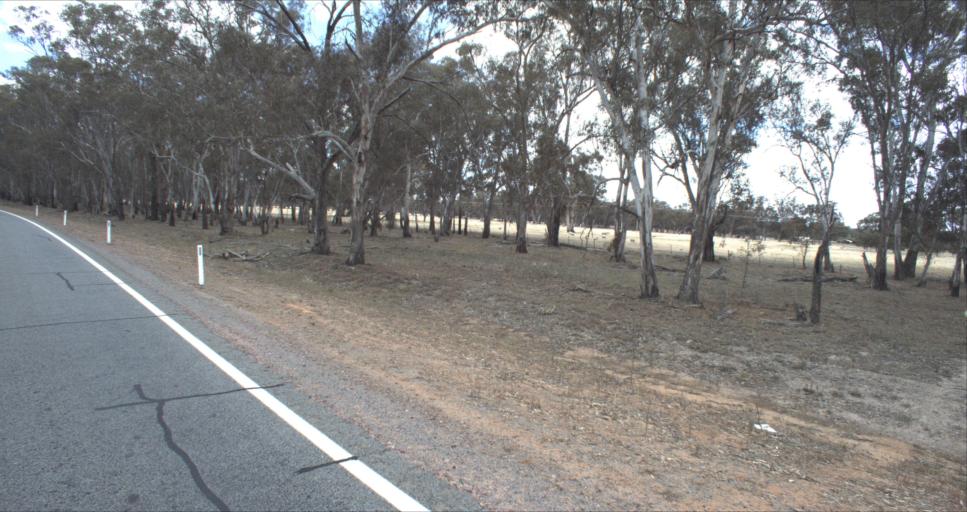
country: AU
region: New South Wales
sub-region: Leeton
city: Leeton
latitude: -34.6303
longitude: 146.3760
